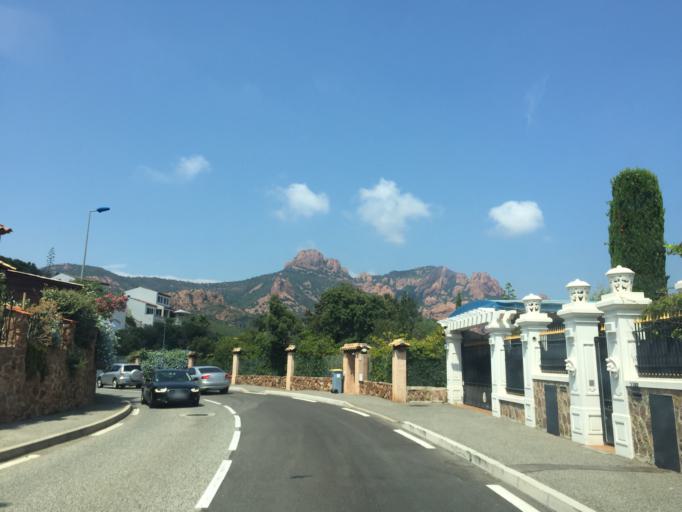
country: FR
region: Provence-Alpes-Cote d'Azur
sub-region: Departement des Alpes-Maritimes
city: Theoule-sur-Mer
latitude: 43.4330
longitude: 6.8944
